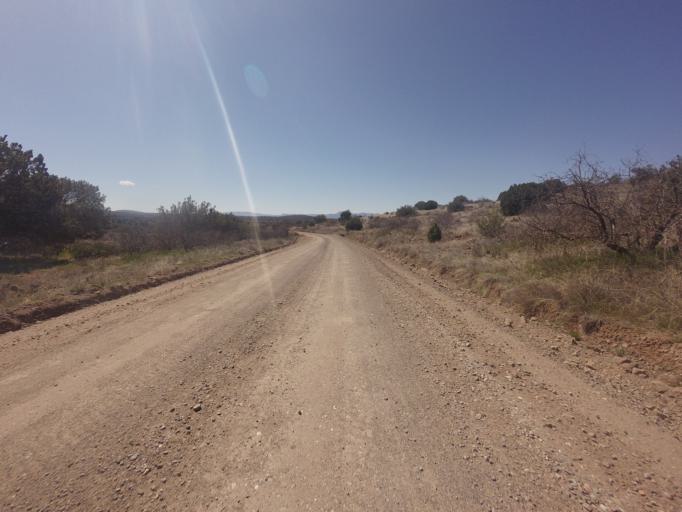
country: US
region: Arizona
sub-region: Yavapai County
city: Lake Montezuma
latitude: 34.6580
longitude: -111.7151
